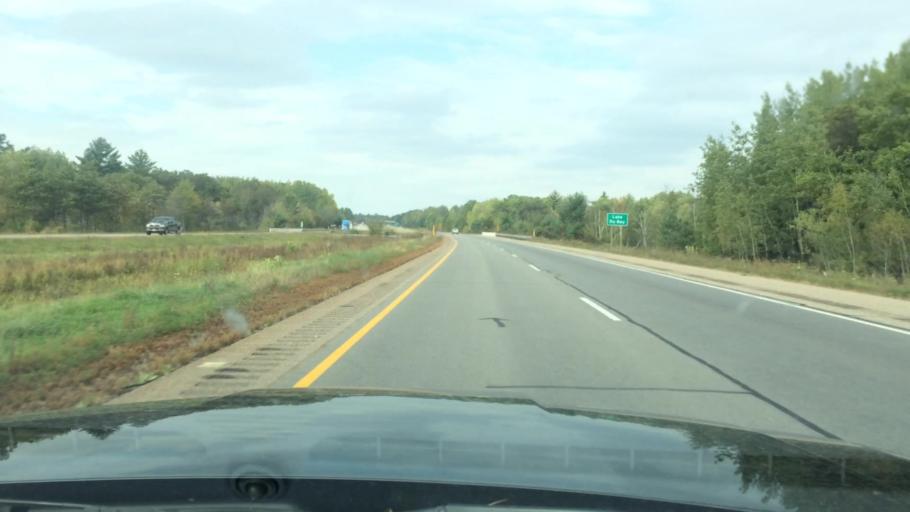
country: US
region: Wisconsin
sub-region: Marathon County
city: Mosinee
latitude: 44.7168
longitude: -89.6628
